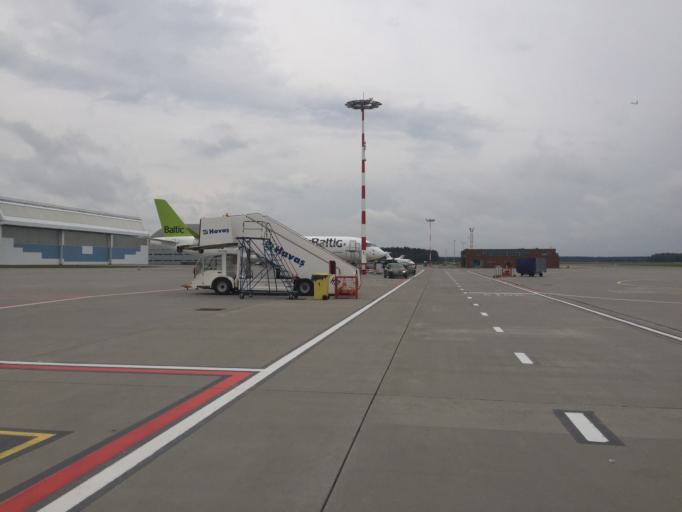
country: LV
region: Babite
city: Pinki
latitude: 56.9183
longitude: 23.9759
